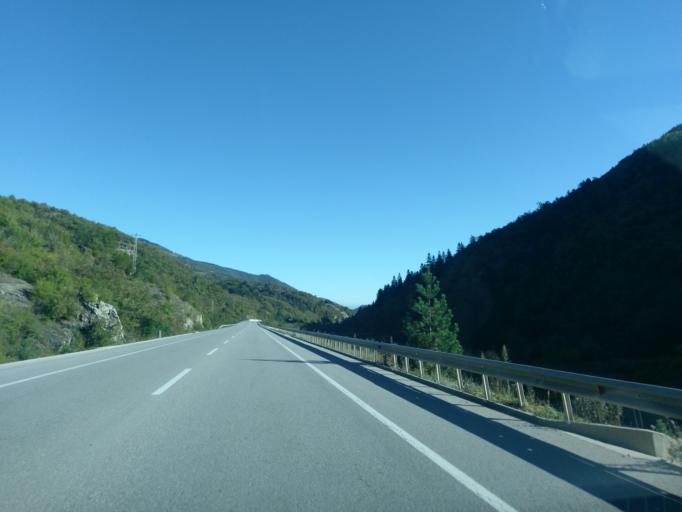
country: TR
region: Sinop
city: Erfelek
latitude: 41.7174
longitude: 34.9358
